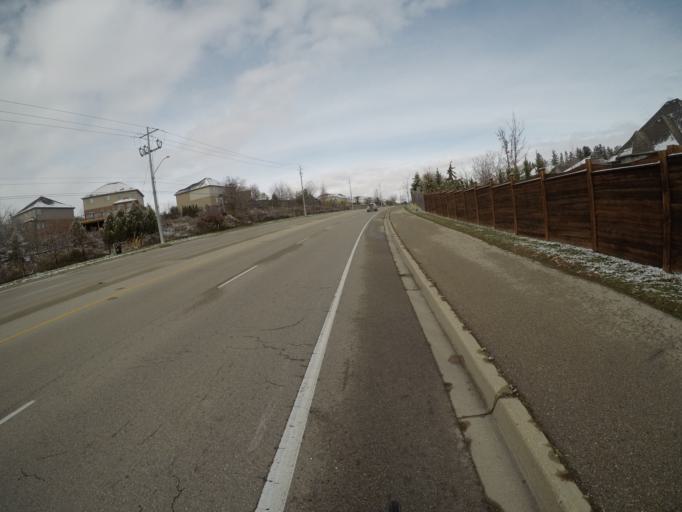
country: CA
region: Ontario
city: Waterloo
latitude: 43.5053
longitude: -80.4970
